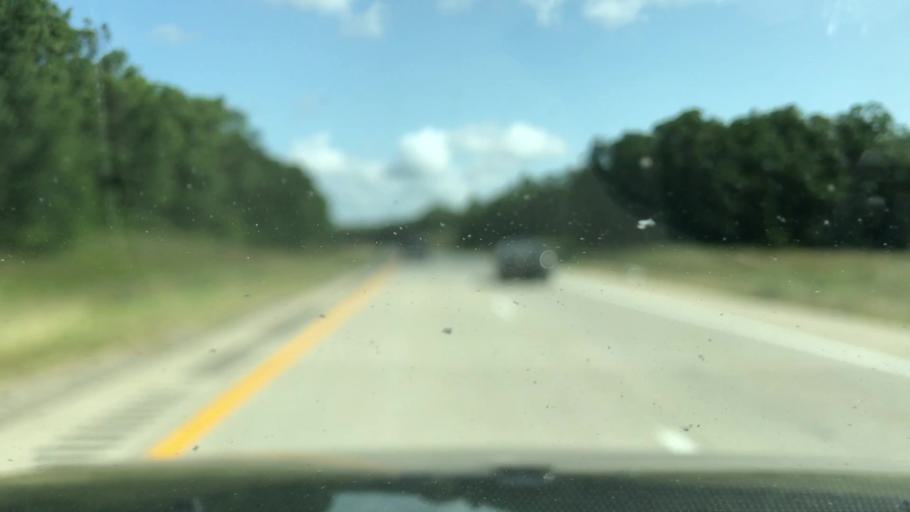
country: US
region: Michigan
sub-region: Montcalm County
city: Howard City
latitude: 43.4213
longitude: -85.4974
